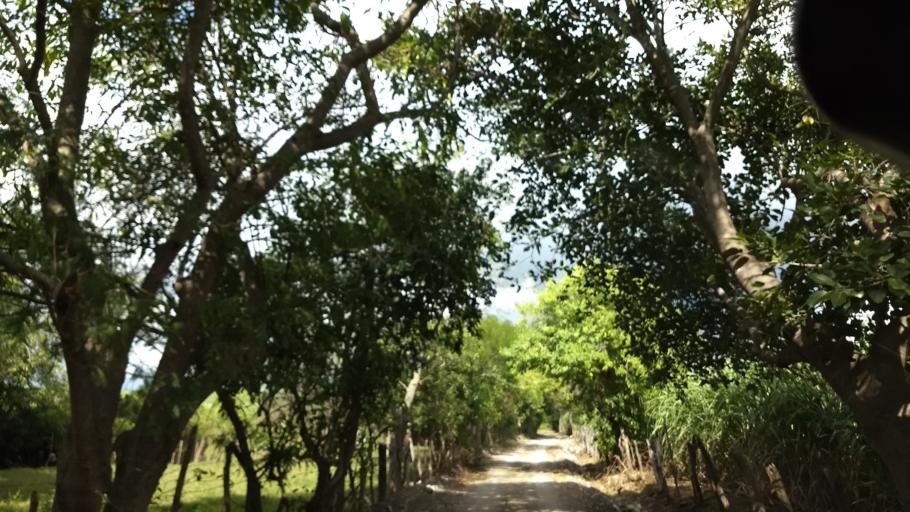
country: MX
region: Colima
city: Suchitlan
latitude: 19.4582
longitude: -103.7663
